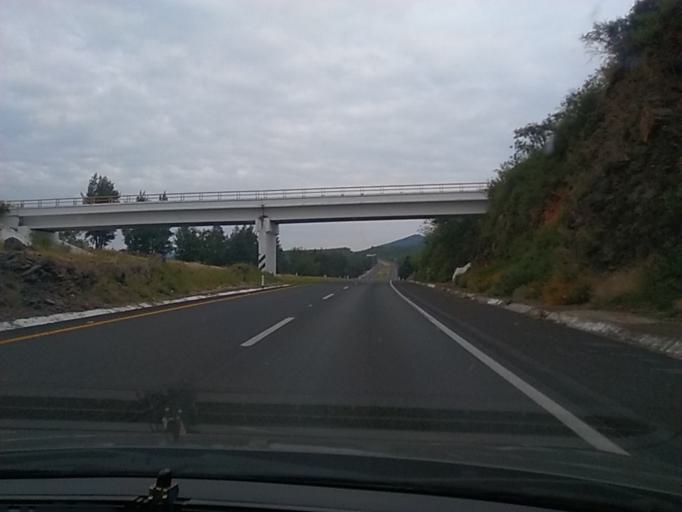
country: MX
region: Michoacan
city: Panindicuaro de la Reforma
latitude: 19.9720
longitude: -101.7231
